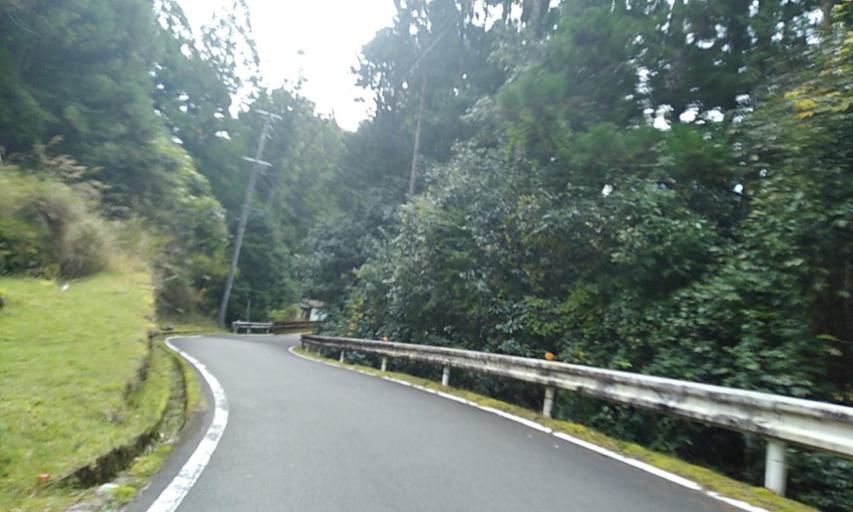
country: JP
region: Wakayama
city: Shingu
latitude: 33.9328
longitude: 135.9787
